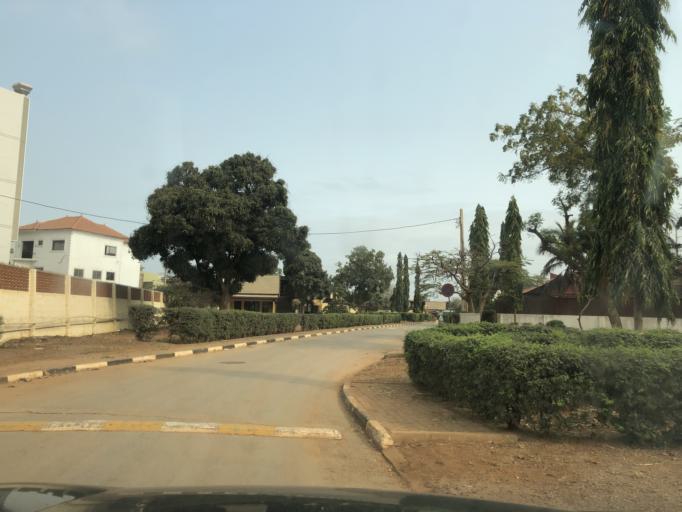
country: AO
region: Luanda
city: Luanda
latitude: -8.9017
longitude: 13.1978
